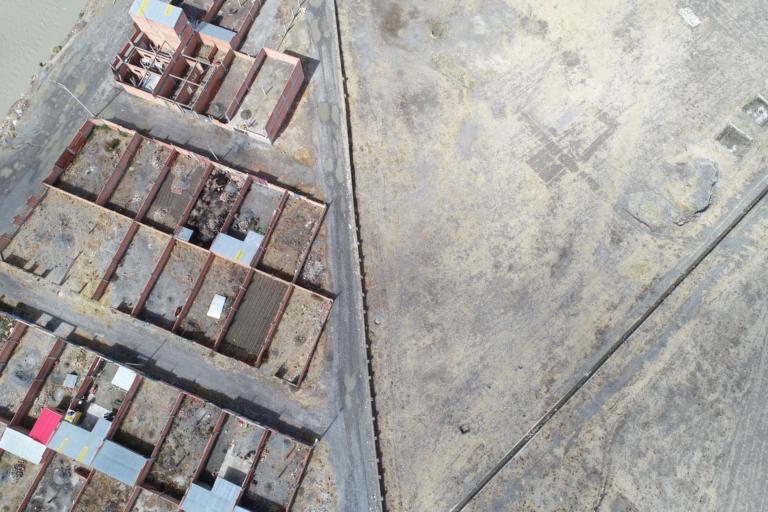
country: BO
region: La Paz
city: Achacachi
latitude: -16.0371
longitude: -68.6855
